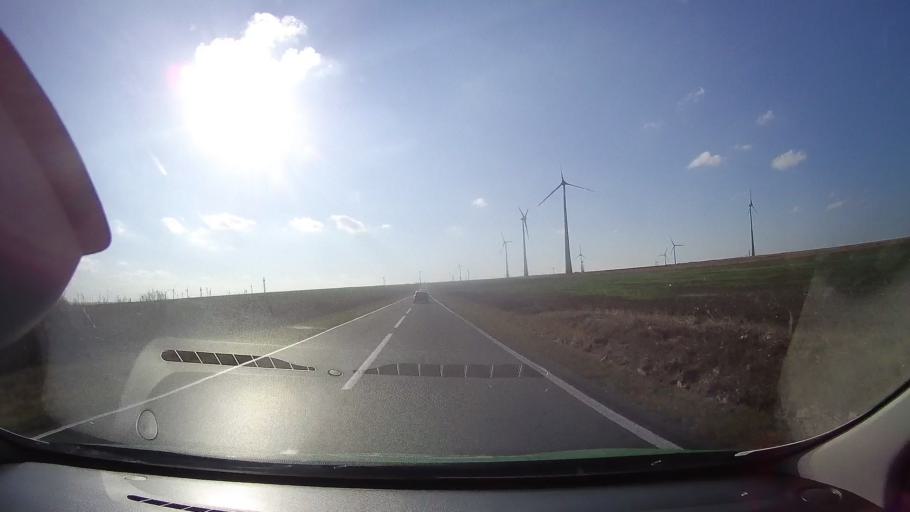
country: RO
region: Tulcea
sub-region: Comuna Topolog
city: Topolog
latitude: 44.8253
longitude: 28.2732
